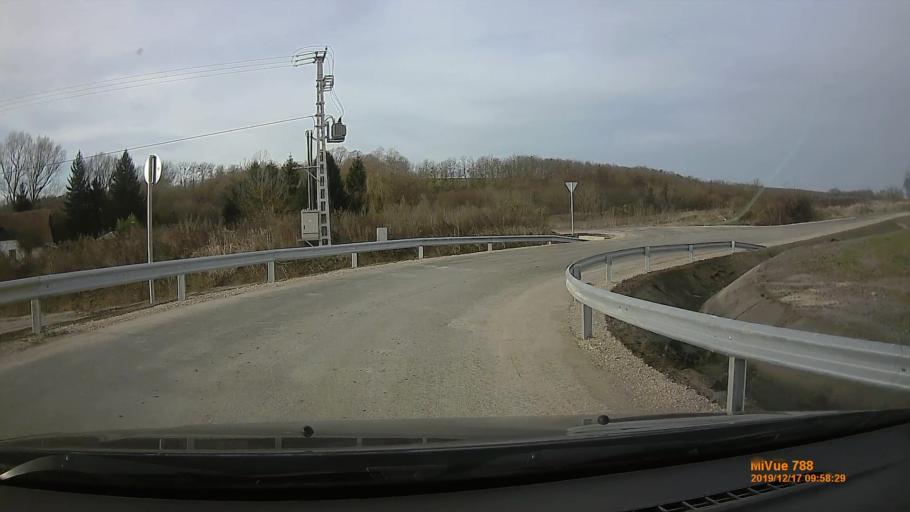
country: HU
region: Somogy
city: Karad
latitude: 46.6239
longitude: 17.7916
